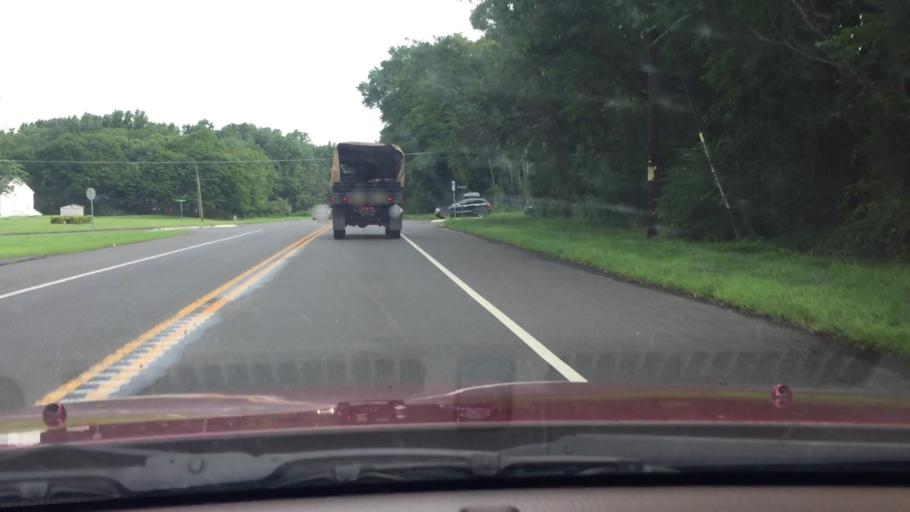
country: US
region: New Jersey
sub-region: Burlington County
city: Fort Dix
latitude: 40.0642
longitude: -74.6529
